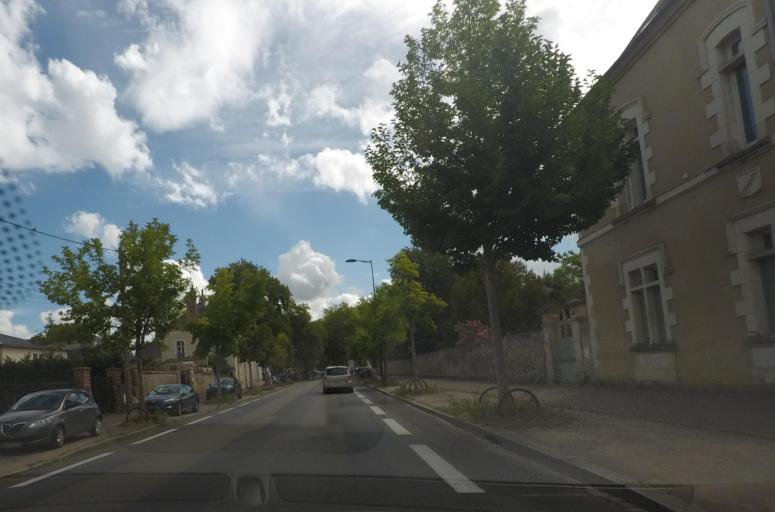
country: FR
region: Pays de la Loire
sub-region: Departement de la Sarthe
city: La Fleche
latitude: 47.6979
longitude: -0.0805
